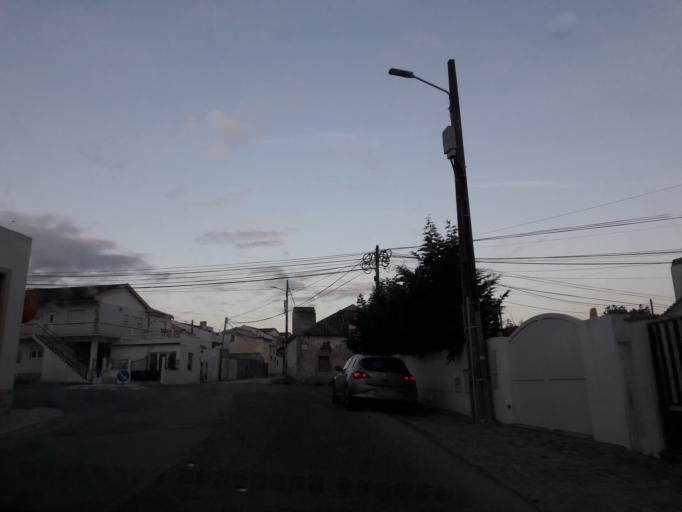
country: PT
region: Leiria
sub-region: Peniche
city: Atouguia da Baleia
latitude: 39.3633
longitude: -9.3155
